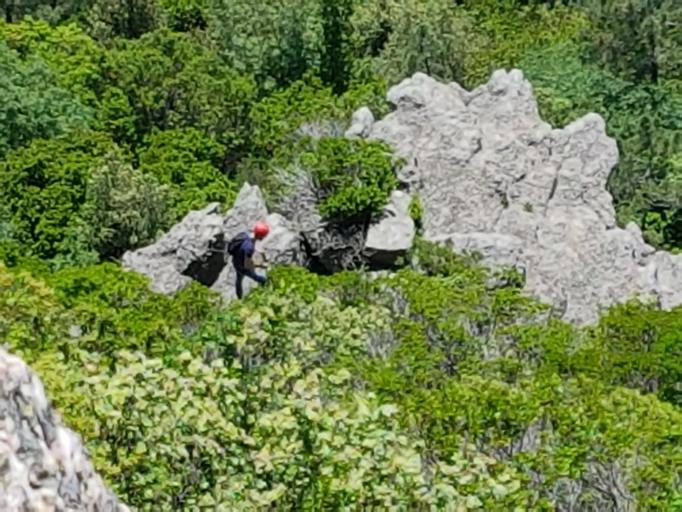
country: IT
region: Tuscany
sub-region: Province of Pisa
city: Buti
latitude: 43.7347
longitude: 10.5600
